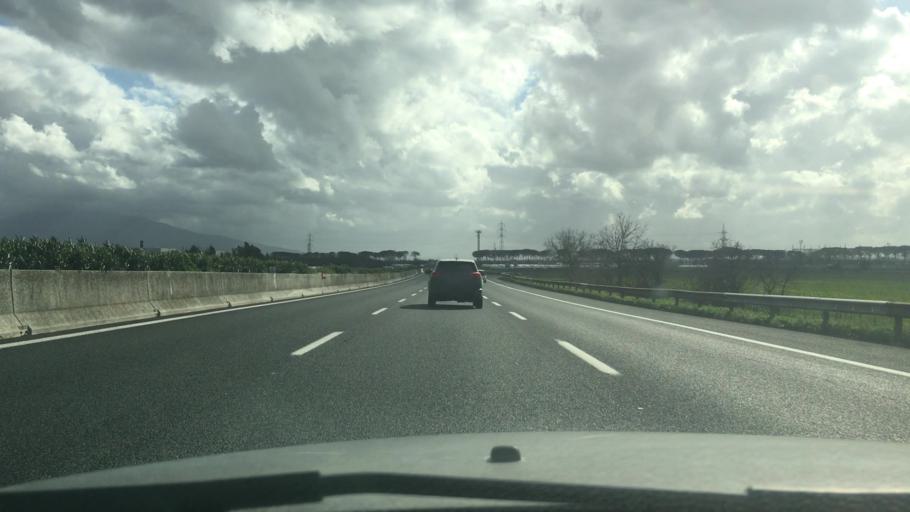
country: IT
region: Campania
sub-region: Provincia di Napoli
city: Pascarola
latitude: 40.9972
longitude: 14.3241
